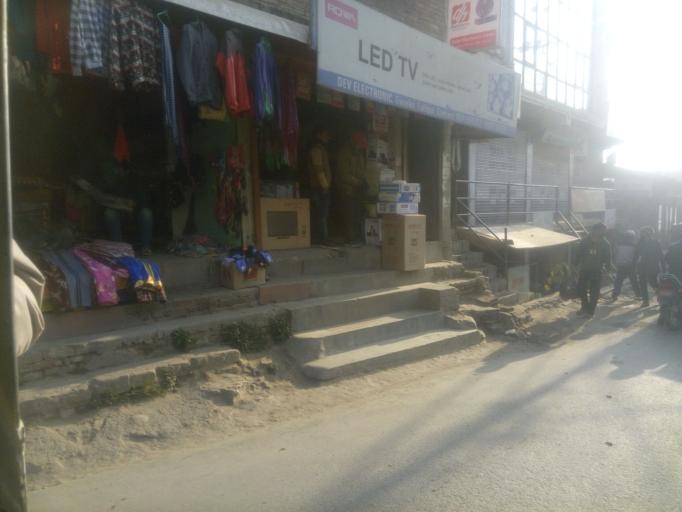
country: NP
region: Central Region
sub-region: Bagmati Zone
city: Patan
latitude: 27.6668
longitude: 85.3319
